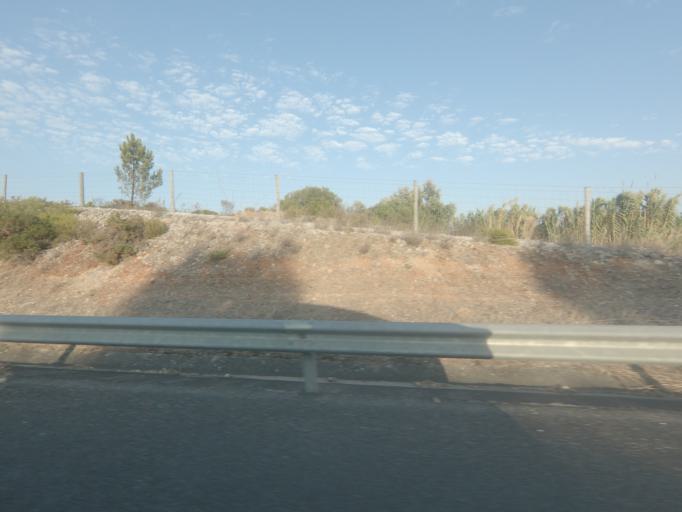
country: PT
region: Santarem
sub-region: Alcanena
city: Alcanena
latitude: 39.4776
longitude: -8.6360
